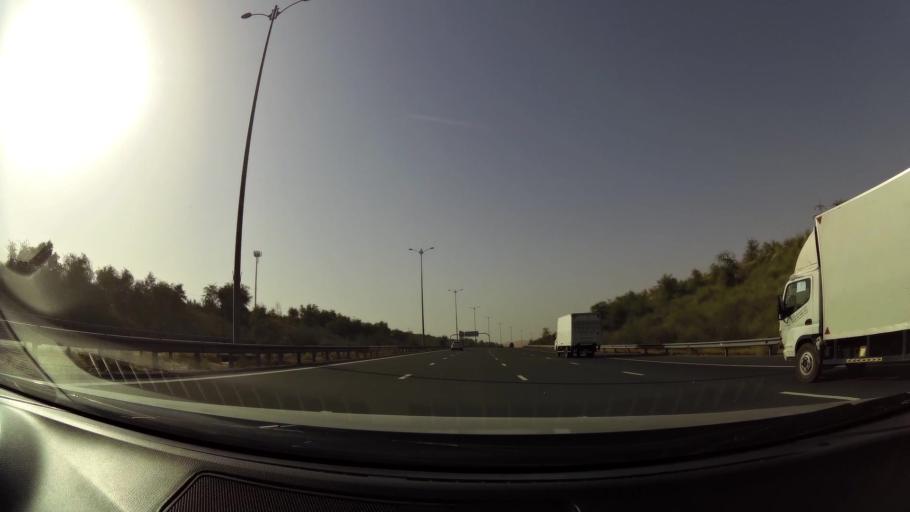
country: OM
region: Al Buraimi
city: Al Buraymi
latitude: 24.6334
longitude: 55.7186
